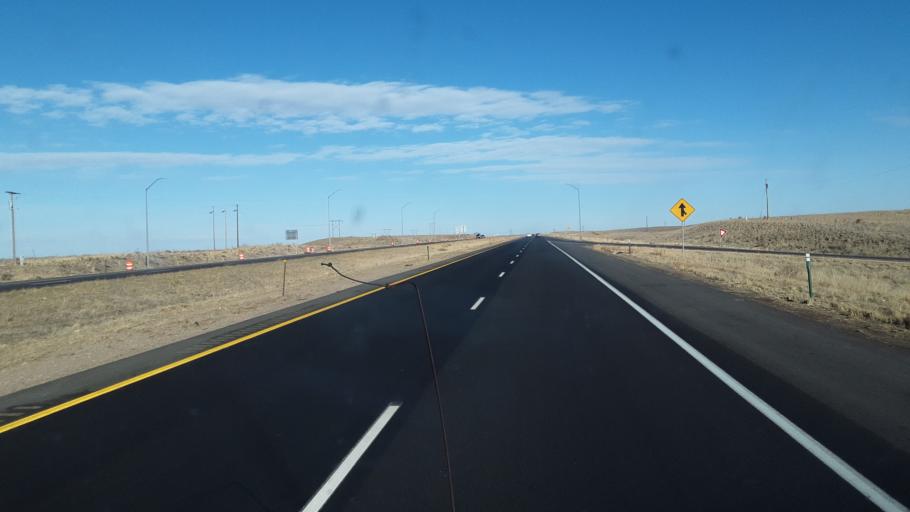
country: US
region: Colorado
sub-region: Morgan County
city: Brush
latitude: 40.2722
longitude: -103.5819
